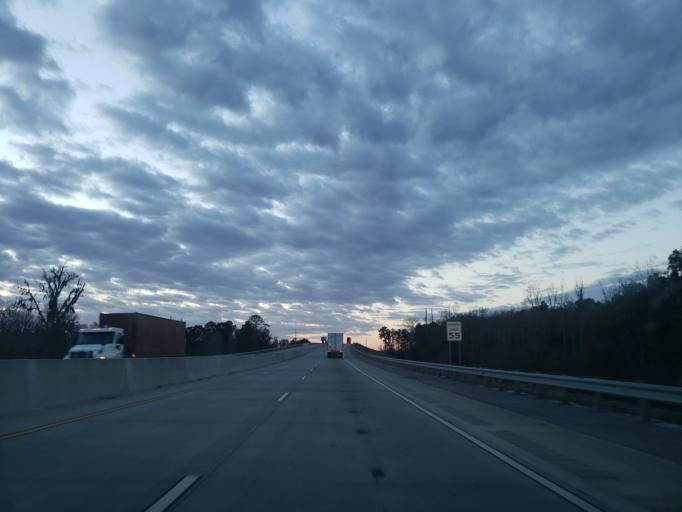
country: US
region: Georgia
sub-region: Chatham County
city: Port Wentworth
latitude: 32.1574
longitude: -81.1769
